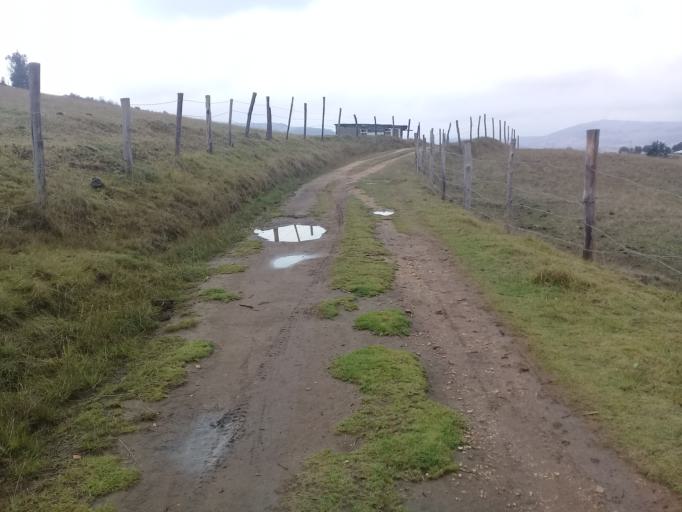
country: CO
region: Boyaca
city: Siachoque
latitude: 5.5647
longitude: -73.2751
